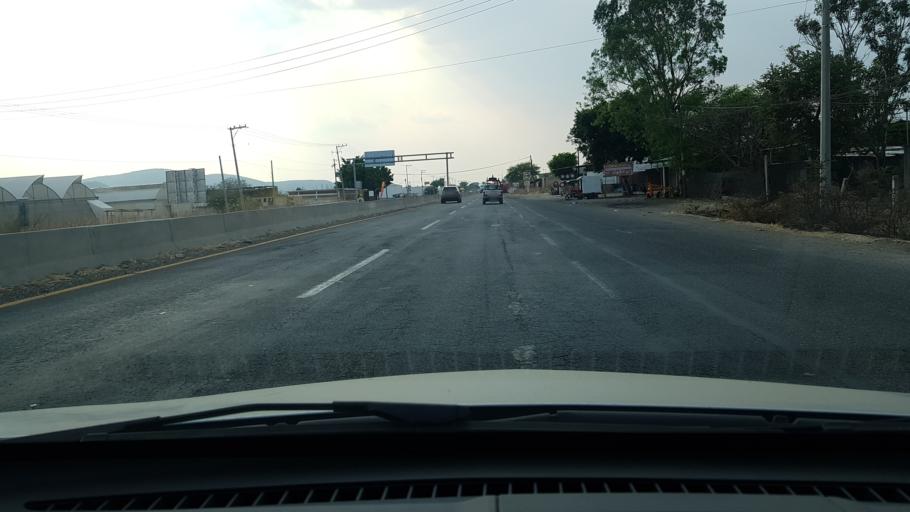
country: MX
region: Morelos
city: Amayuca
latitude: 18.7323
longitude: -98.8143
